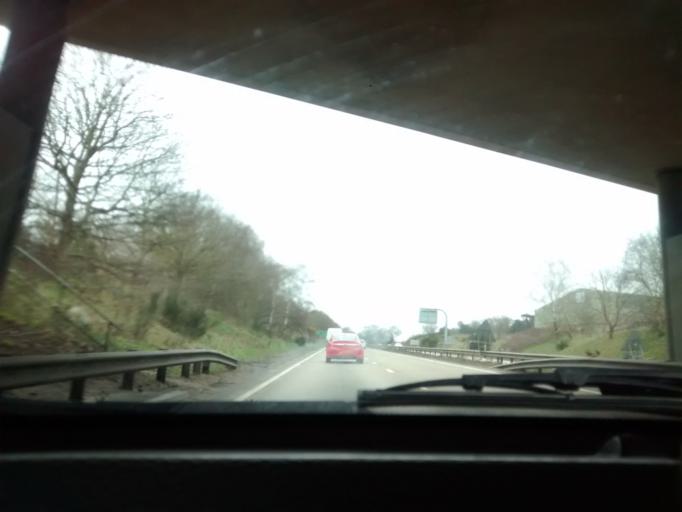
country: GB
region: England
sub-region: Suffolk
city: Kesgrave
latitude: 52.0262
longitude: 1.2384
